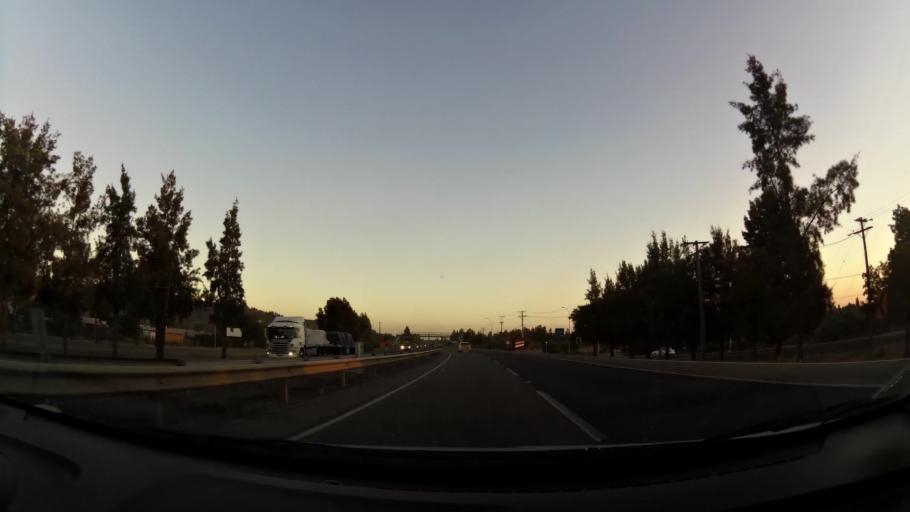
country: CL
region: Maule
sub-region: Provincia de Linares
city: Linares
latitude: -35.7622
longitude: -71.6708
